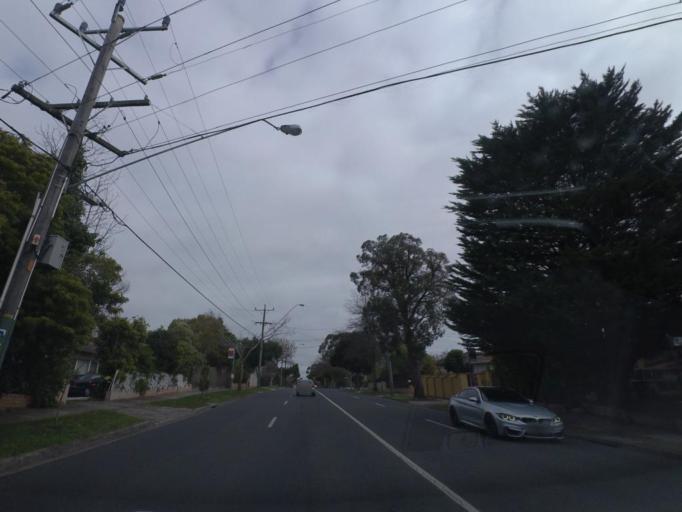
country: AU
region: Victoria
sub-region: Whitehorse
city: Mont Albert North
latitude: -37.8005
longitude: 145.1142
